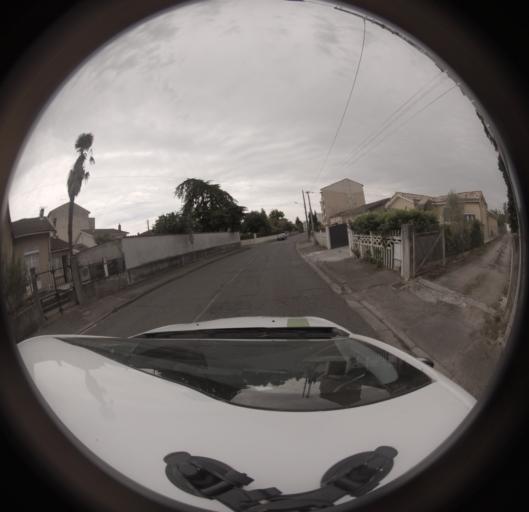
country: FR
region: Midi-Pyrenees
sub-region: Departement du Tarn-et-Garonne
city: Montauban
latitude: 44.0190
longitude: 1.3726
